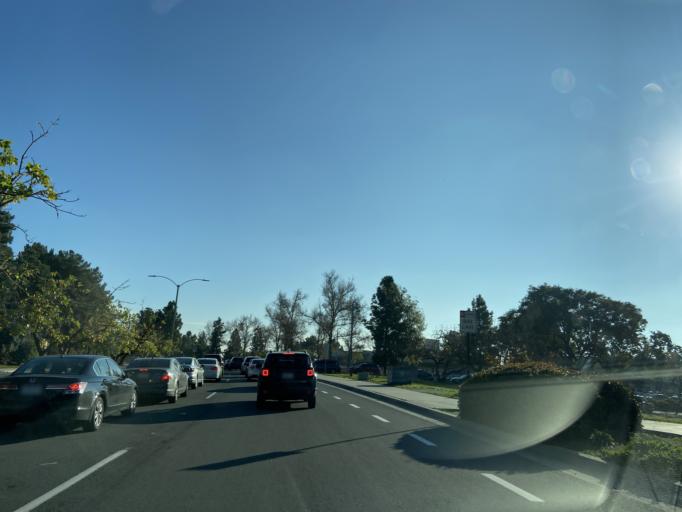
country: US
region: California
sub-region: San Diego County
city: Bonita
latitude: 32.6434
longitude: -116.9667
